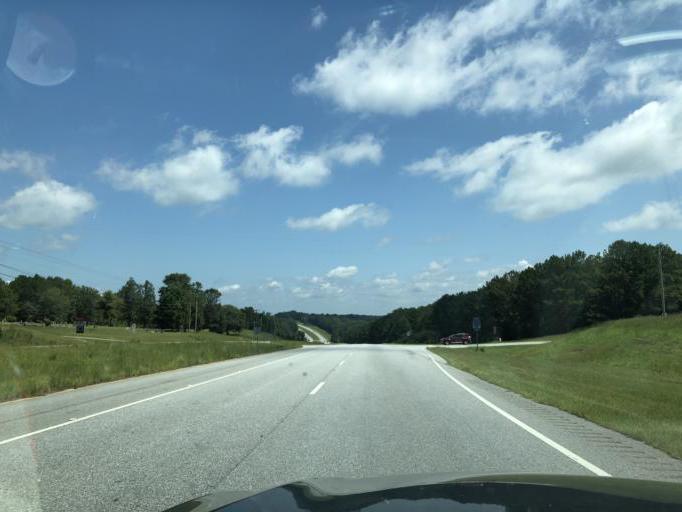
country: US
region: Alabama
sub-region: Barbour County
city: Eufaula
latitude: 31.7678
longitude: -85.1915
